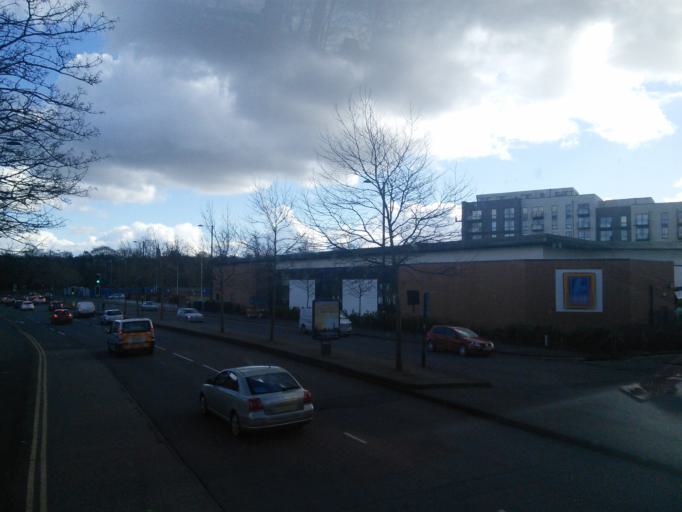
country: GB
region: England
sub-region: City and Borough of Birmingham
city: Birmingham
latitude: 52.4553
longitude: -1.9062
